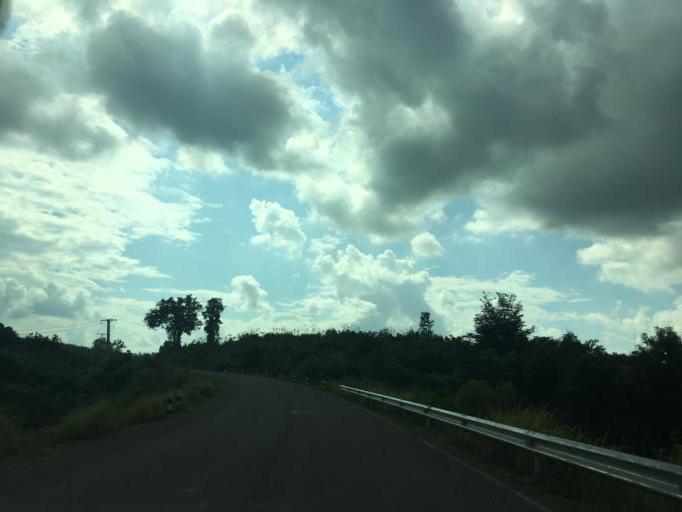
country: TH
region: Nong Khai
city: Sangkhom
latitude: 18.1923
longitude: 102.2143
